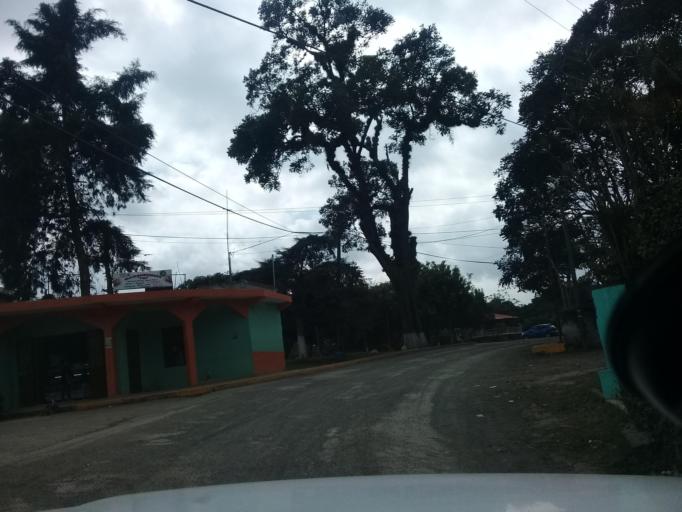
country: MX
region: Veracruz
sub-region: Xalapa
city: Fraccionamiento las Fuentes
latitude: 19.4747
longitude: -96.8798
